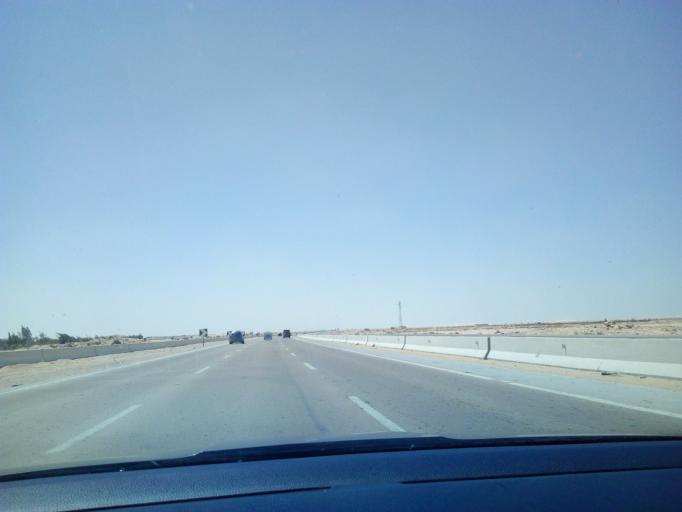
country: EG
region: Al Buhayrah
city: Abu al Matamir
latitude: 30.5826
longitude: 29.9030
